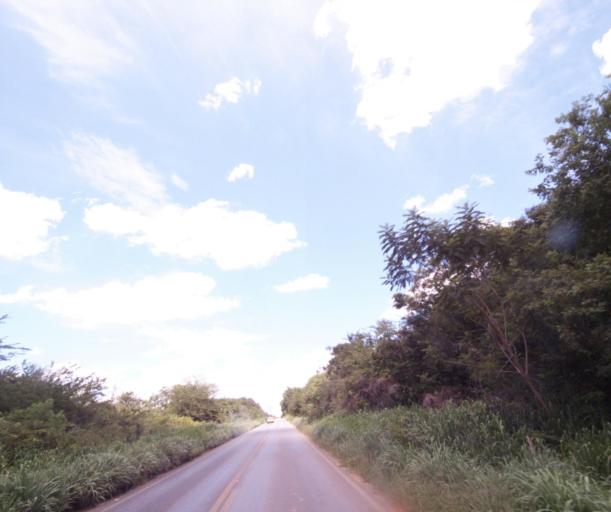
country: BR
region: Bahia
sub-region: Bom Jesus Da Lapa
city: Bom Jesus da Lapa
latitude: -13.2662
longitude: -43.6038
